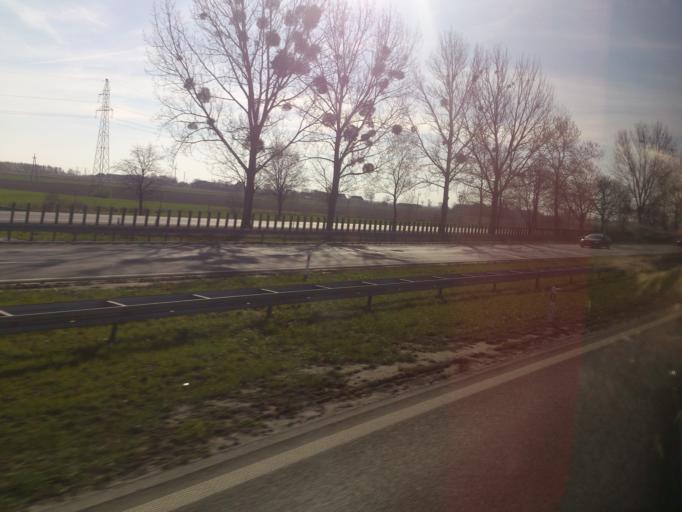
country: PL
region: Kujawsko-Pomorskie
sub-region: Powiat aleksandrowski
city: Raciazek
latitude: 52.8366
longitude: 18.7968
